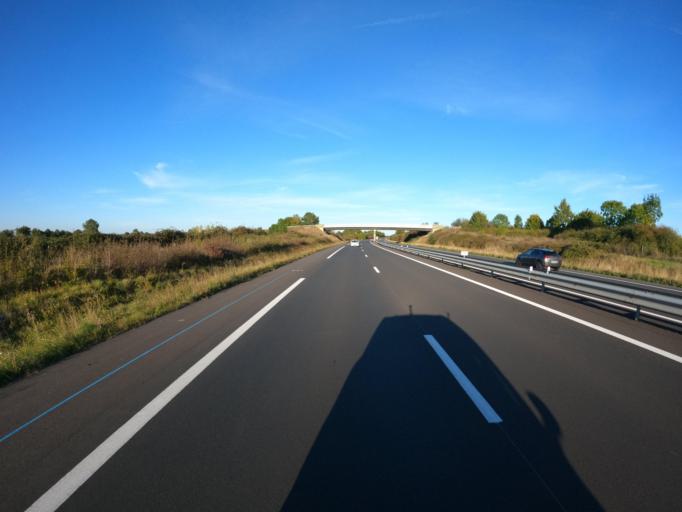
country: FR
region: Pays de la Loire
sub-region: Departement de la Vendee
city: Beaurepaire
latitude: 46.8923
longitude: -1.0937
